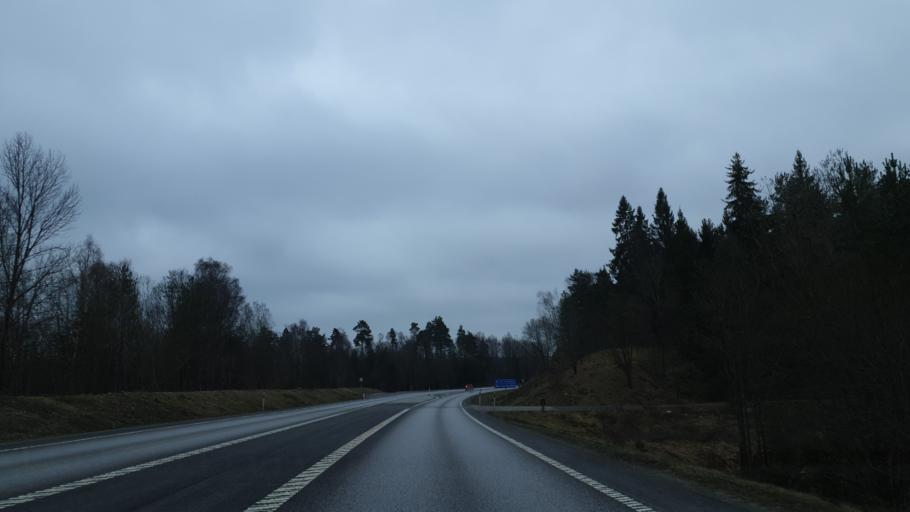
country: SE
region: Vaestra Goetaland
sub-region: Boras Kommun
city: Viskafors
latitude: 57.5899
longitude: 12.8654
